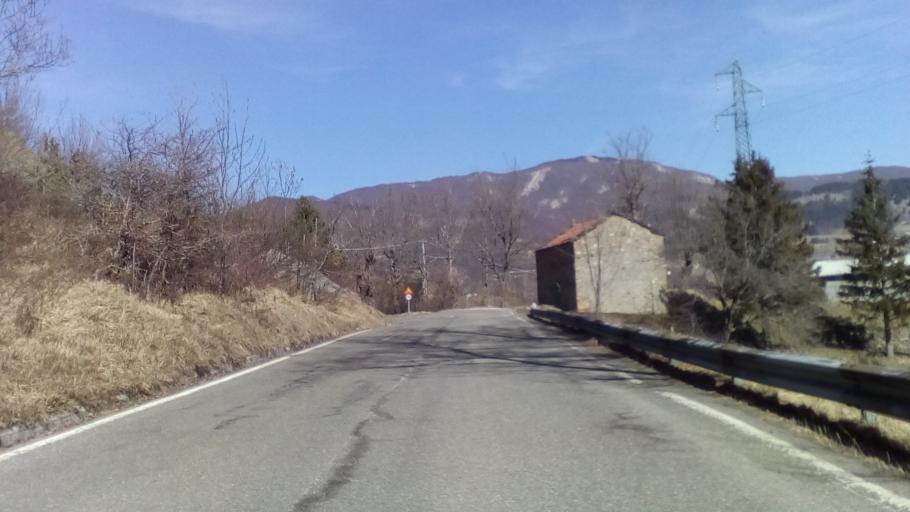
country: IT
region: Emilia-Romagna
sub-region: Provincia di Modena
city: Riolunato
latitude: 44.2408
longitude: 10.6341
